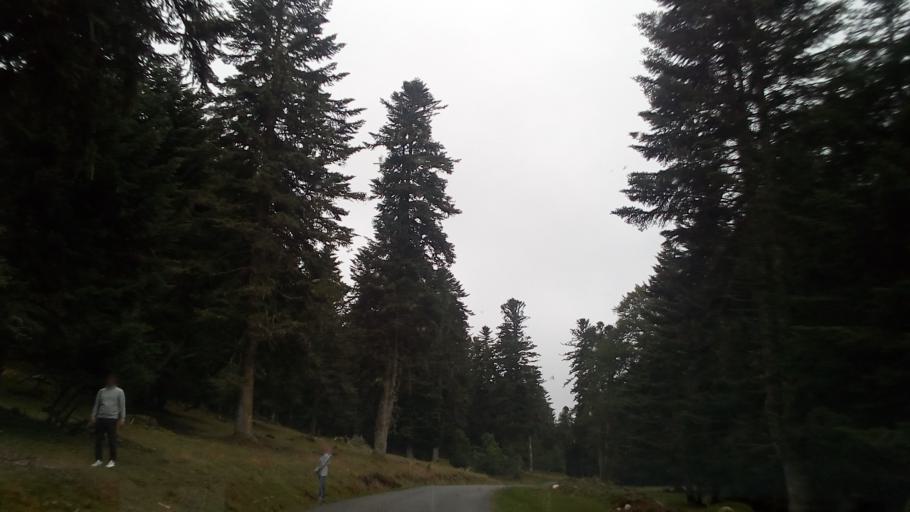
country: FR
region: Midi-Pyrenees
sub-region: Departement des Hautes-Pyrenees
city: Saint-Lary-Soulan
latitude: 42.9280
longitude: 0.2939
